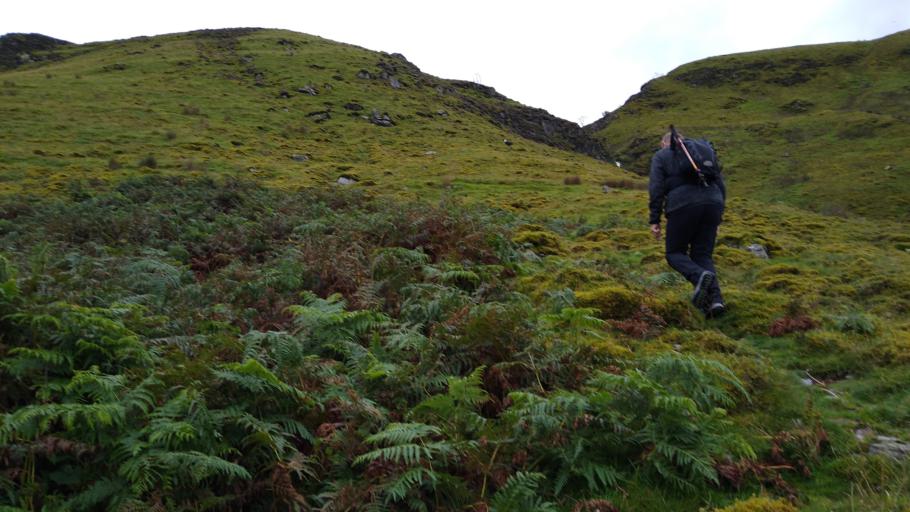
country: GB
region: England
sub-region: Cumbria
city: Keswick
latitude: 54.6752
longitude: -3.1443
